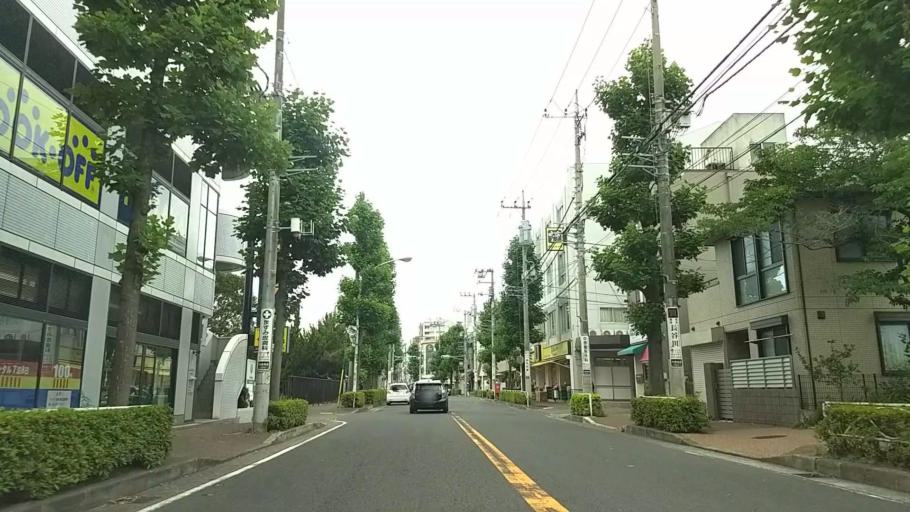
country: JP
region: Kanagawa
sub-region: Kawasaki-shi
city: Kawasaki
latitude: 35.5811
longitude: 139.6456
